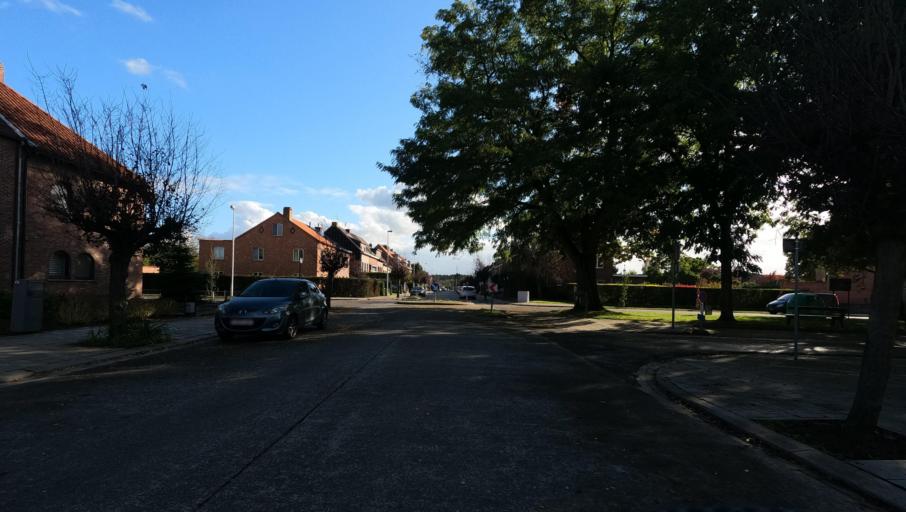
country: BE
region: Flanders
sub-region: Provincie Antwerpen
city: Wijnegem
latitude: 51.2279
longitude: 4.5096
